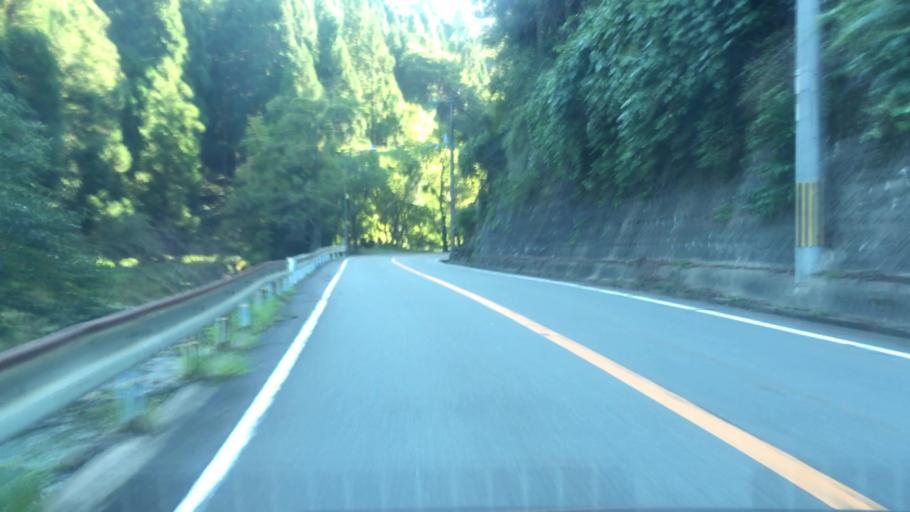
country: JP
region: Hyogo
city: Toyooka
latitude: 35.6193
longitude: 134.8611
